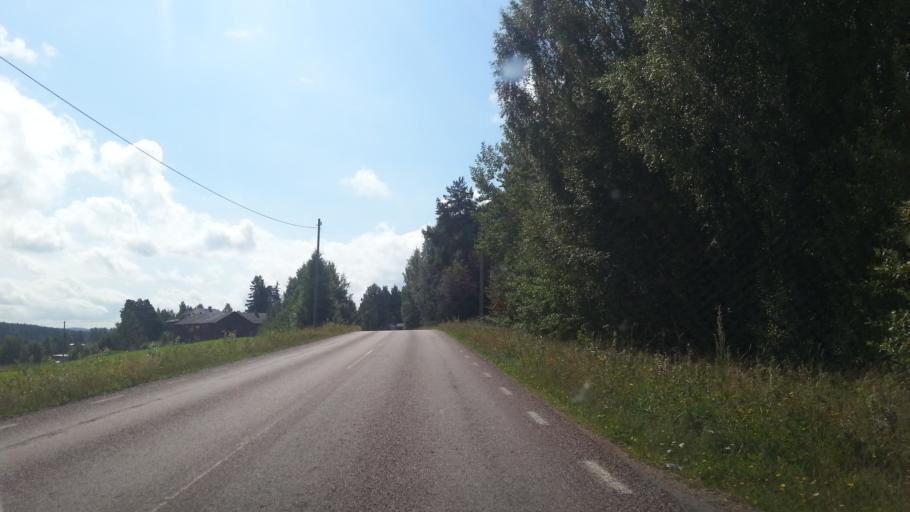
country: SE
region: Dalarna
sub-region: Faluns Kommun
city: Falun
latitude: 60.6243
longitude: 15.7677
